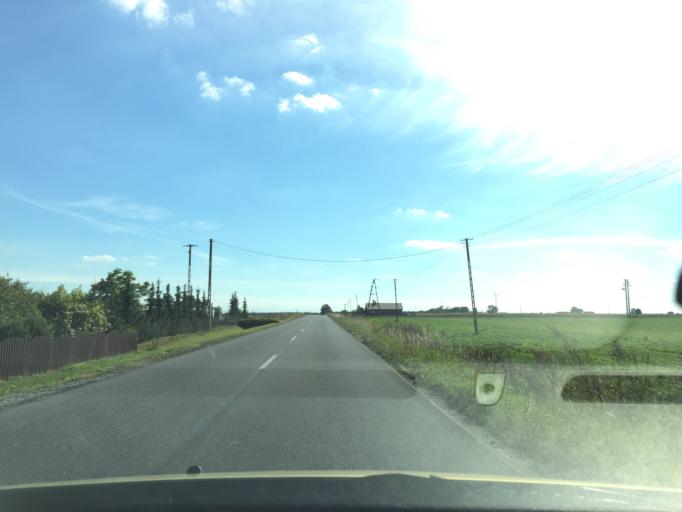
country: PL
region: Greater Poland Voivodeship
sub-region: Powiat kaliski
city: Stawiszyn
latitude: 51.9389
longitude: 18.1495
